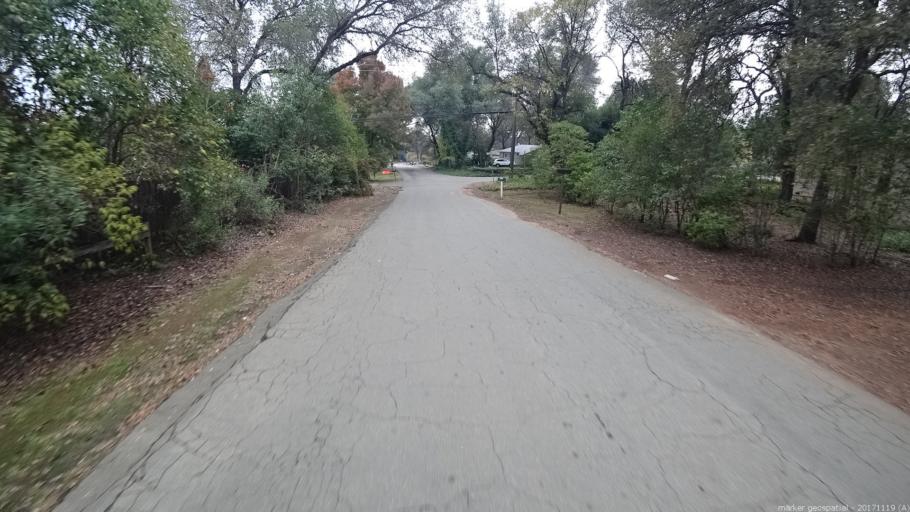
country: US
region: California
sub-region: Shasta County
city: Anderson
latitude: 40.4904
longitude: -122.3730
